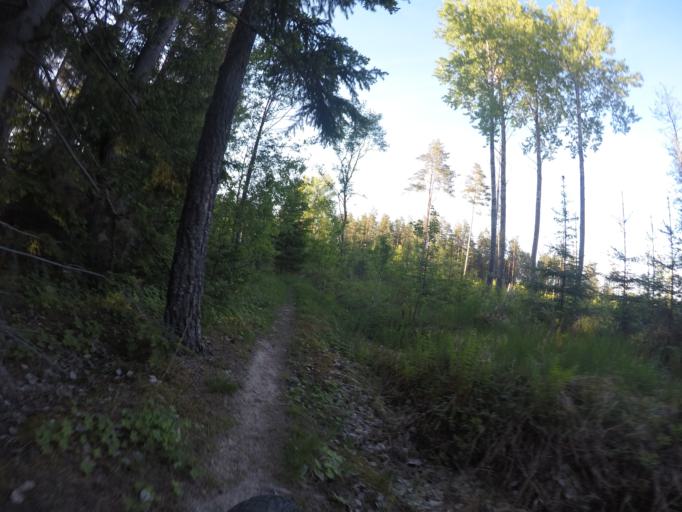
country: SE
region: Soedermanland
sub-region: Eskilstuna Kommun
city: Eskilstuna
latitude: 59.3302
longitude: 16.5256
